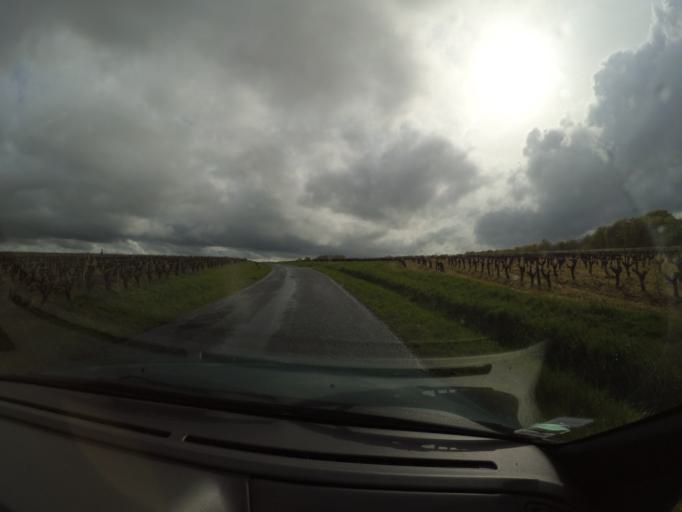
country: FR
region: Pays de la Loire
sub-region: Departement de la Loire-Atlantique
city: Monnieres
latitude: 47.1224
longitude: -1.3563
